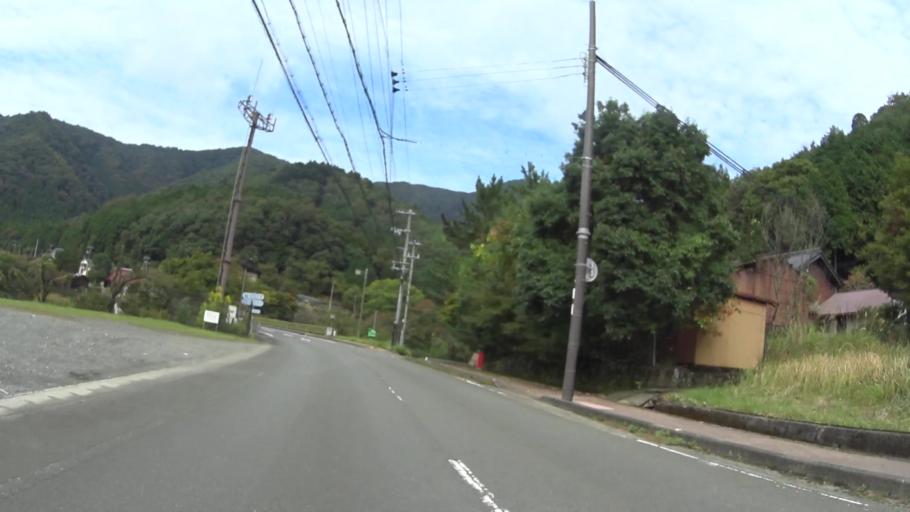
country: JP
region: Kyoto
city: Ayabe
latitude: 35.2702
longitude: 135.4716
